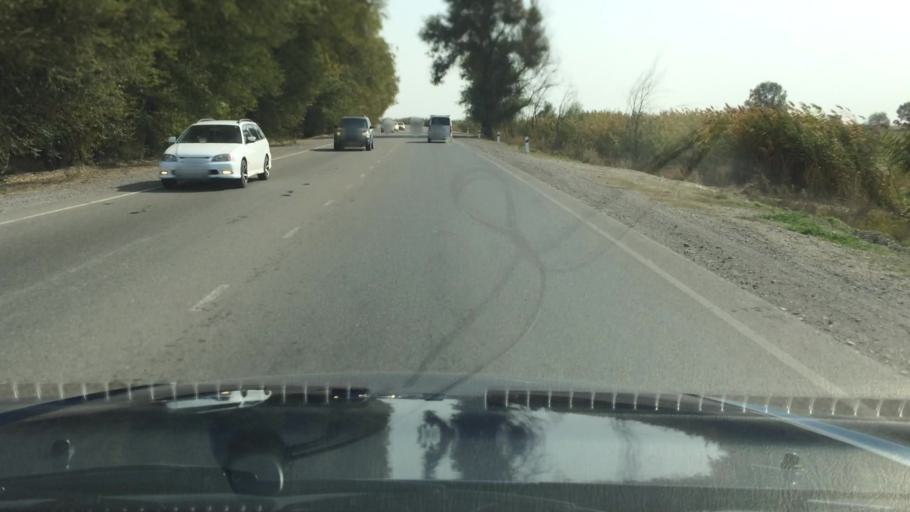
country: KG
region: Chuy
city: Lebedinovka
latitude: 42.9210
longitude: 74.7096
